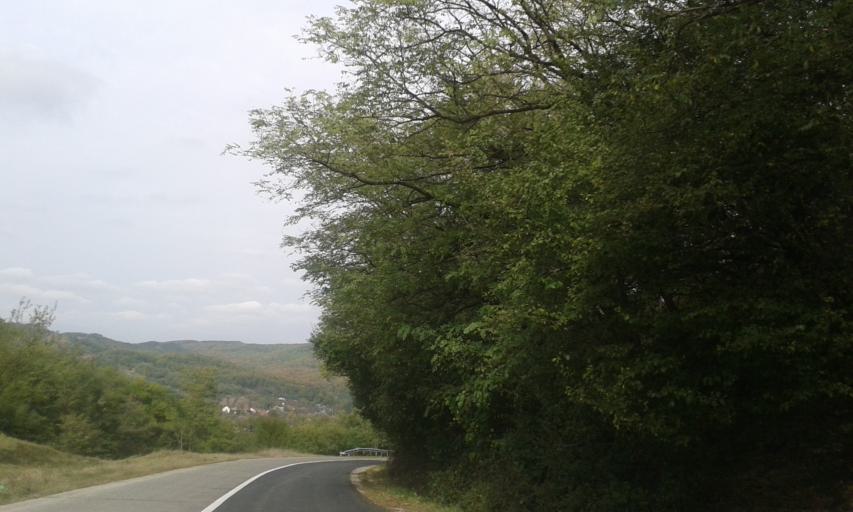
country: RO
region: Gorj
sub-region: Comuna Stejari
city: Piscoiu
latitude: 44.9131
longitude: 23.7707
